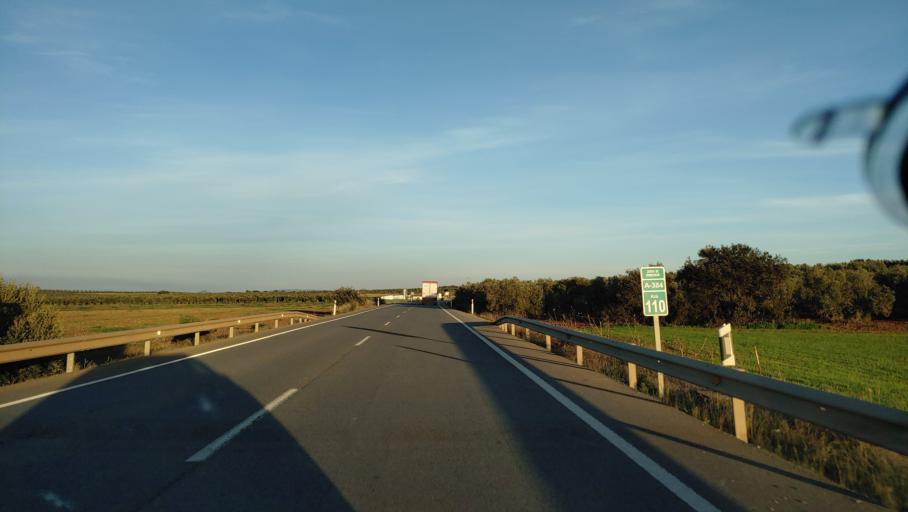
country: ES
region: Andalusia
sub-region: Provincia de Malaga
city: Campillos
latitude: 37.0488
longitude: -4.8282
